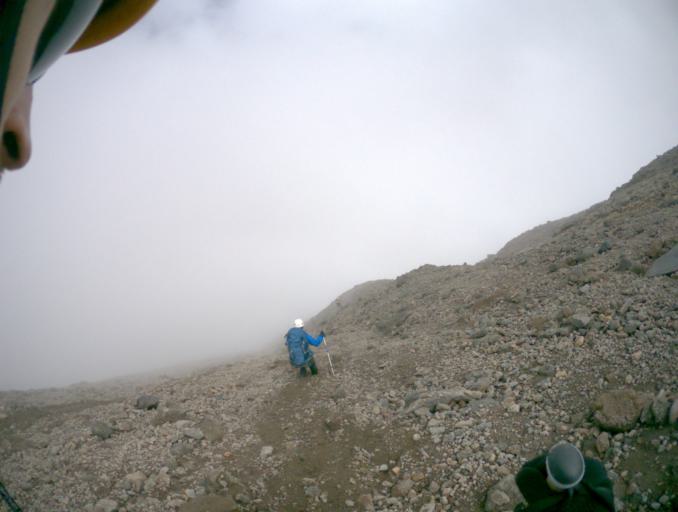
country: RU
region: Kabardino-Balkariya
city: Terskol
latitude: 43.3806
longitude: 42.4098
